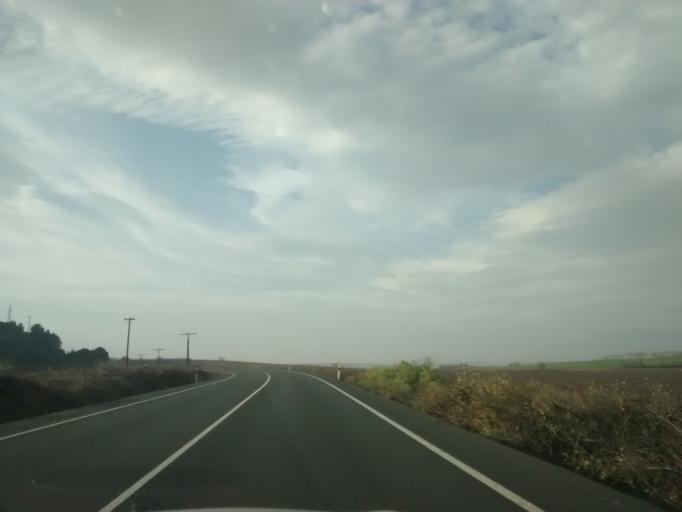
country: ES
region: La Rioja
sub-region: Provincia de La Rioja
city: Torremontalbo
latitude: 42.5053
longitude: -2.6922
